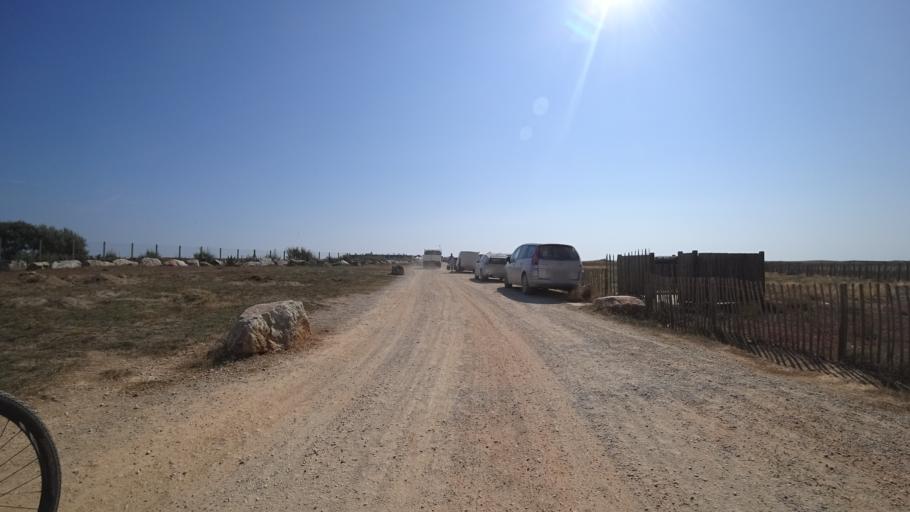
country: FR
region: Languedoc-Roussillon
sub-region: Departement des Pyrenees-Orientales
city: Le Barcares
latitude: 42.7580
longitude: 3.0359
